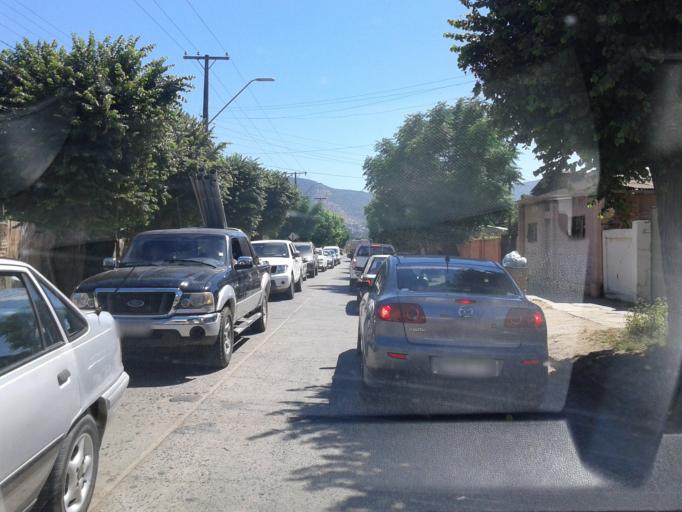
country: CL
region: Valparaiso
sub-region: Provincia de Marga Marga
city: Limache
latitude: -33.0099
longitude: -71.2515
